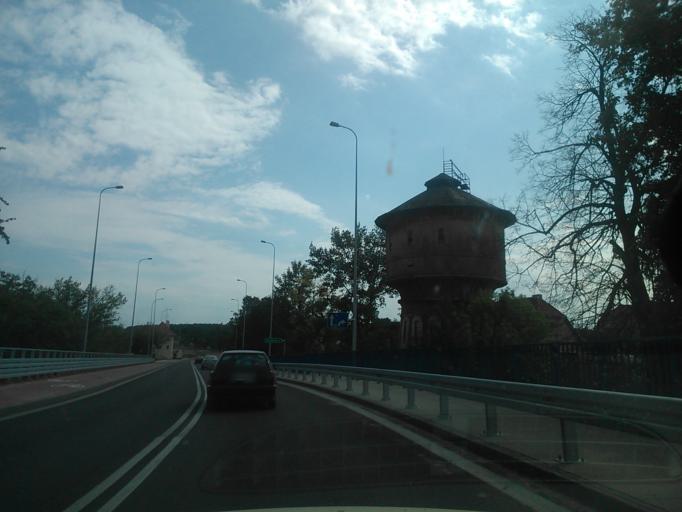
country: PL
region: Warmian-Masurian Voivodeship
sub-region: Powiat dzialdowski
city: Ilowo -Osada
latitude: 53.1652
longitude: 20.2932
